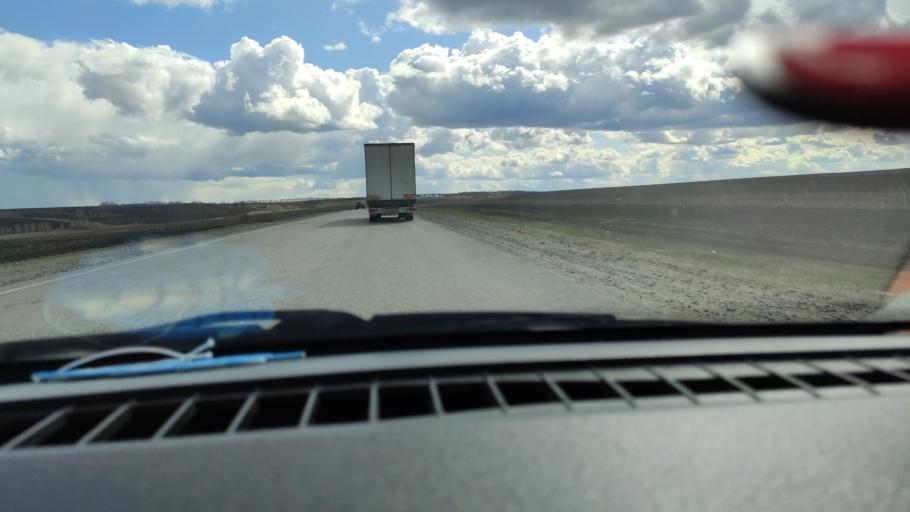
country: RU
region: Samara
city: Varlamovo
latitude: 53.0137
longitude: 48.3325
